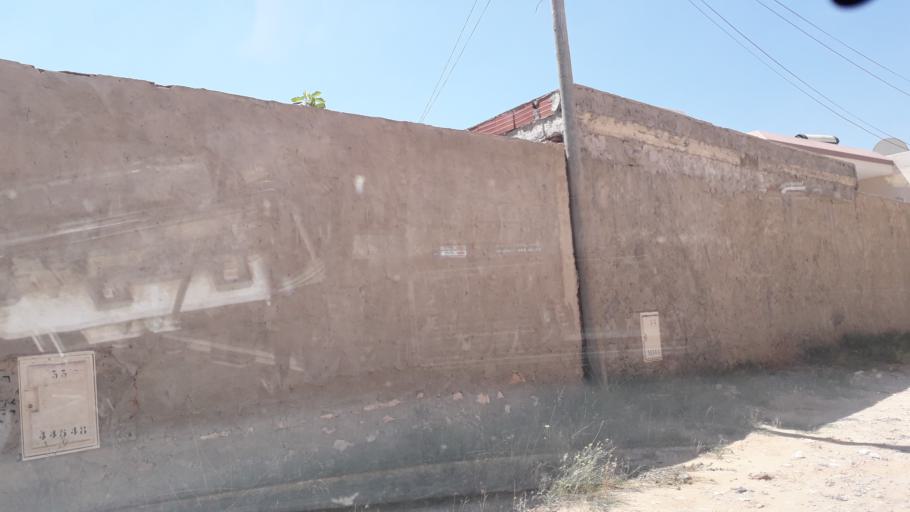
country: TN
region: Safaqis
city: Al Qarmadah
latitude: 34.8238
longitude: 10.7654
